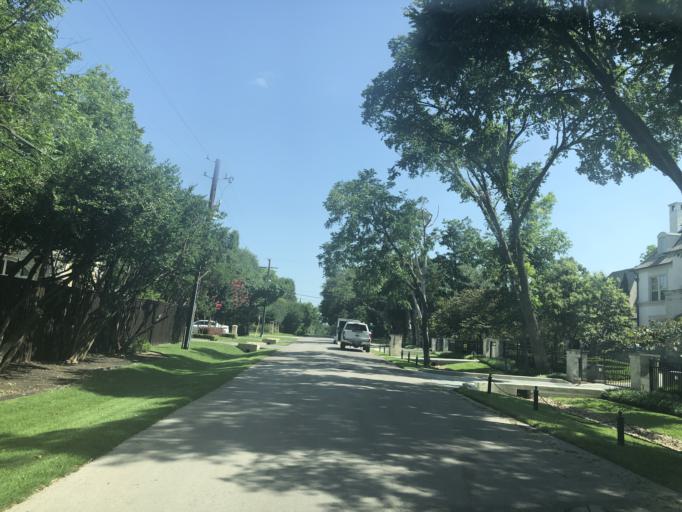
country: US
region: Texas
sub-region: Dallas County
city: University Park
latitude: 32.8778
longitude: -96.8139
